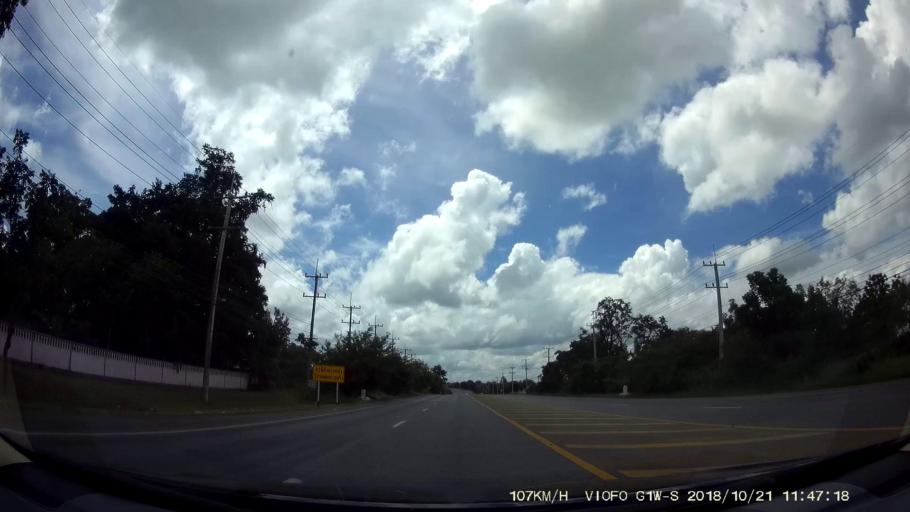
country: TH
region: Chaiyaphum
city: Noen Sa-nga
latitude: 15.6633
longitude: 101.9553
